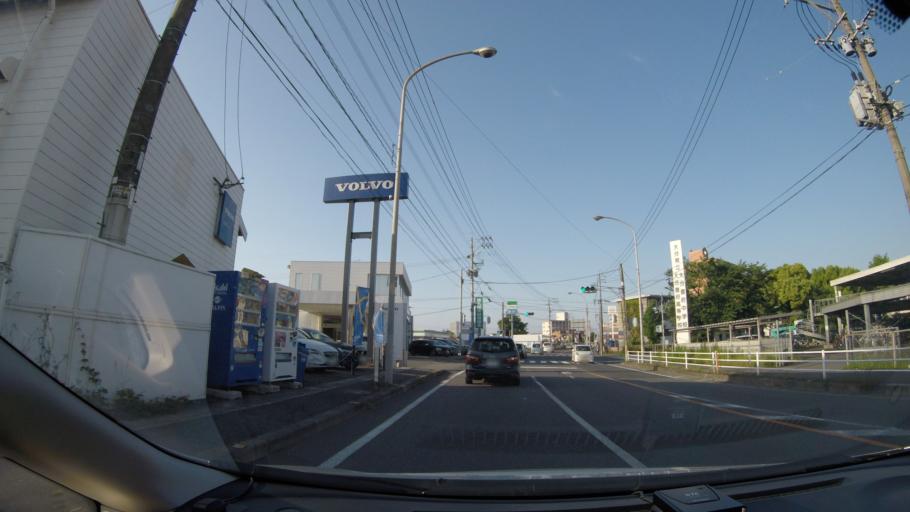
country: JP
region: Oita
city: Oita
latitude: 33.2069
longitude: 131.6035
